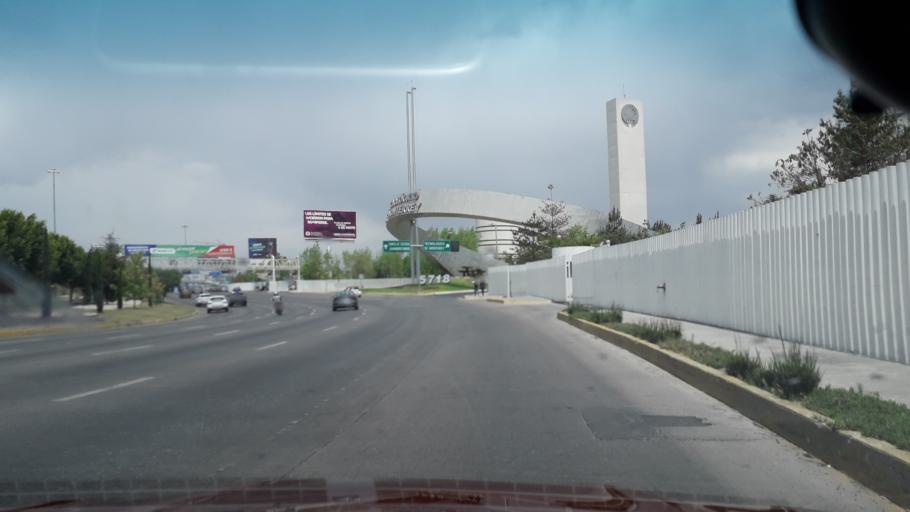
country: MX
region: Puebla
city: Tlazcalancingo
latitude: 19.0201
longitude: -98.2458
